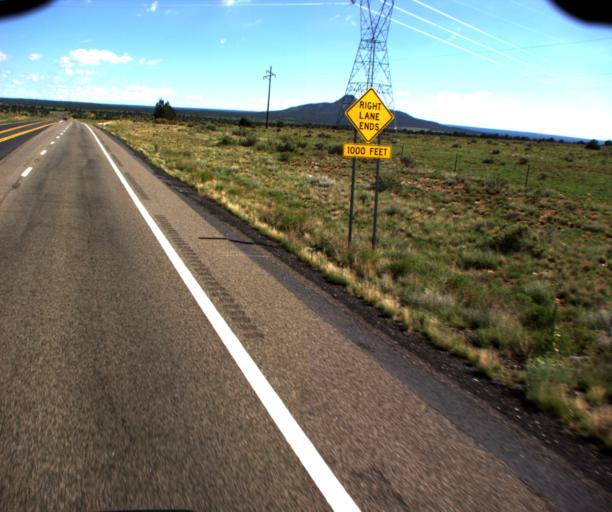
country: US
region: Arizona
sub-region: Coconino County
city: Grand Canyon Village
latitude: 35.7643
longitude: -112.1306
